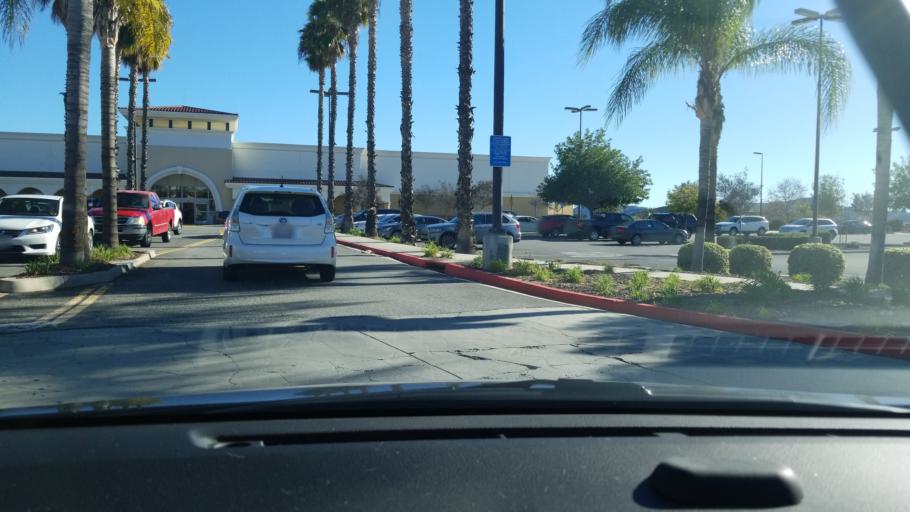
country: US
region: California
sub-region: Riverside County
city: Murrieta
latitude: 33.5626
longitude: -117.2089
